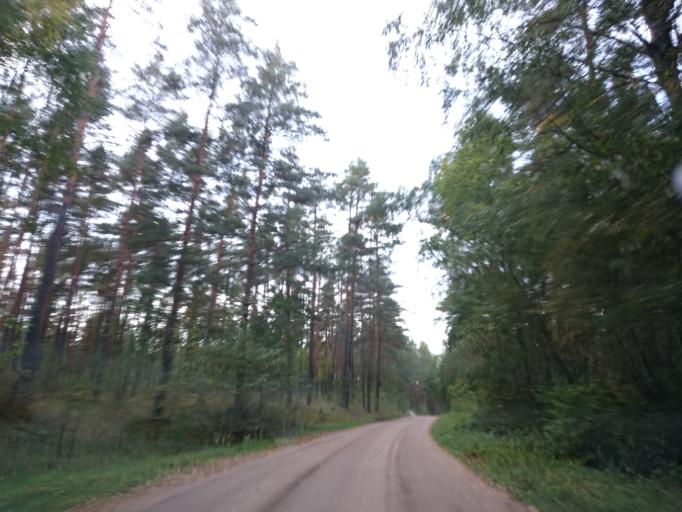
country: LV
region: Garkalne
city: Garkalne
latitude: 57.0552
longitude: 24.3742
